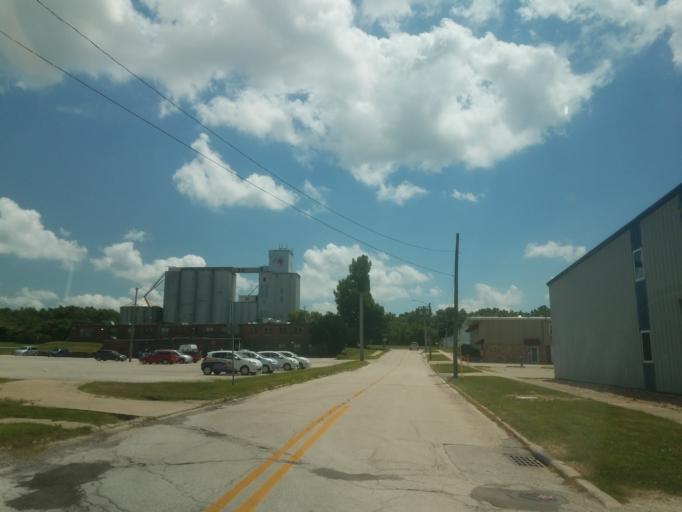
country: US
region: Illinois
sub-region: McLean County
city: Bloomington
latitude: 40.4805
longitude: -89.0136
